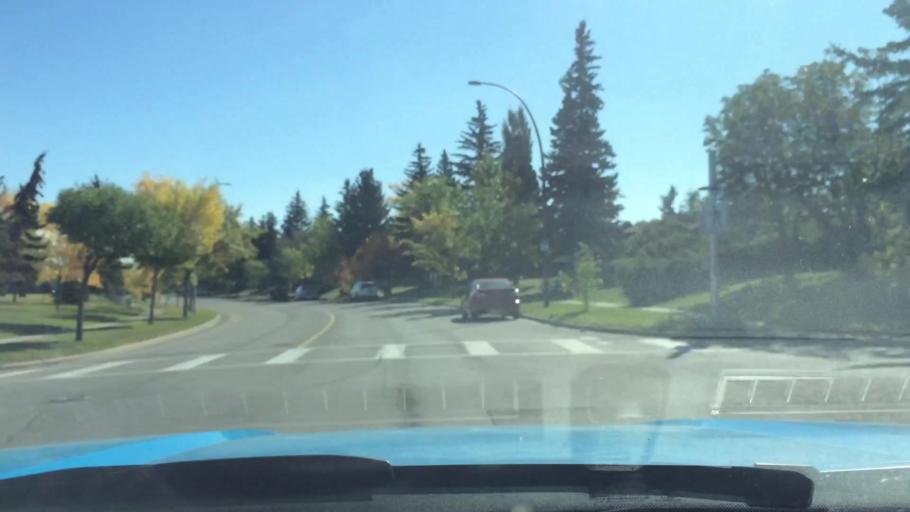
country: CA
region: Alberta
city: Calgary
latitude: 51.1180
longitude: -114.0635
